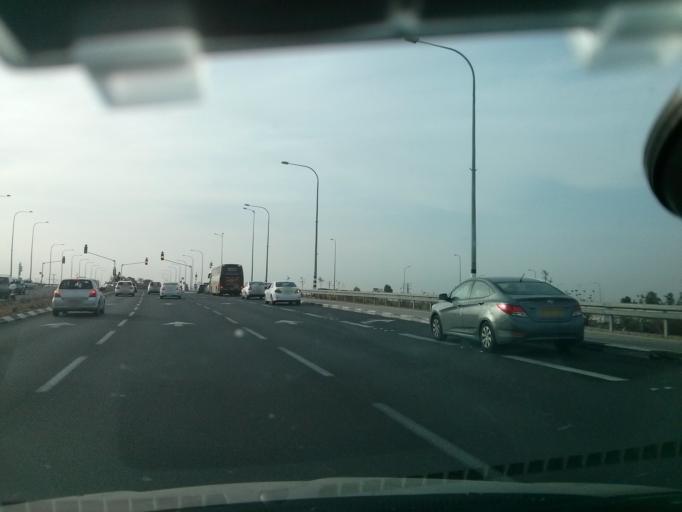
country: IL
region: Central District
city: Bene 'Ayish
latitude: 31.7950
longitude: 34.7677
